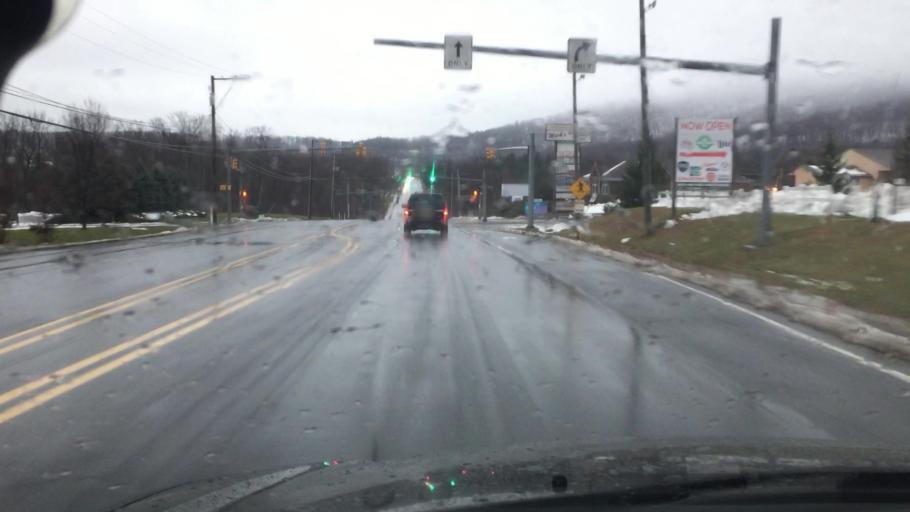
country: US
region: Pennsylvania
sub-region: Luzerne County
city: Harleigh
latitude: 41.0103
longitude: -75.9659
